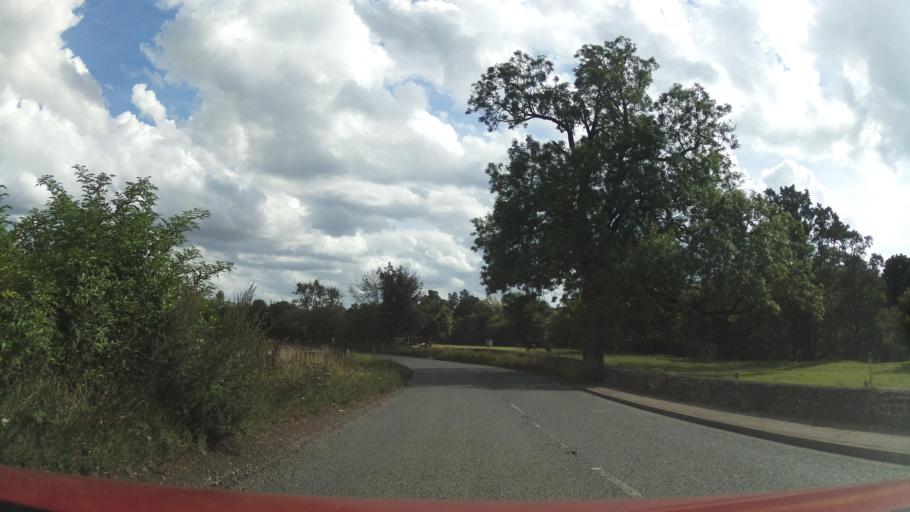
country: GB
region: England
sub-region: North Yorkshire
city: Bedale
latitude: 54.2260
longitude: -1.6538
